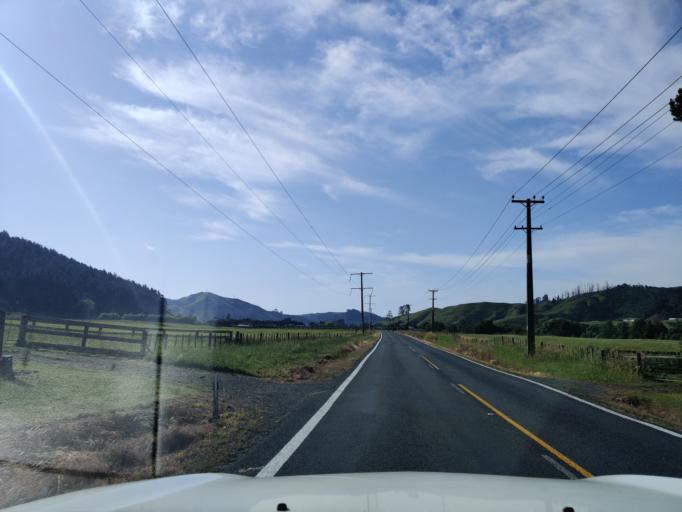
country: NZ
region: Waikato
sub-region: Waikato District
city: Ngaruawahia
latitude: -37.6109
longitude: 175.1784
